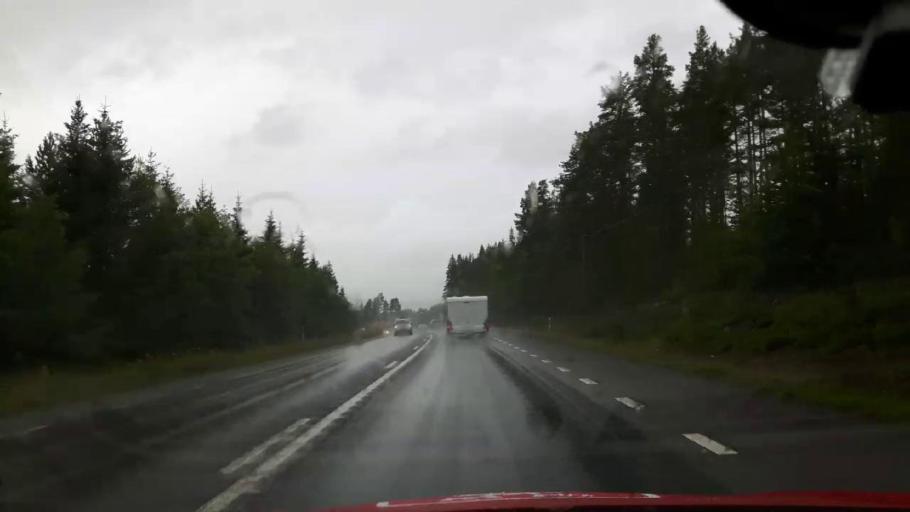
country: SE
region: Jaemtland
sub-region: Are Kommun
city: Jarpen
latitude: 63.3399
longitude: 13.4921
